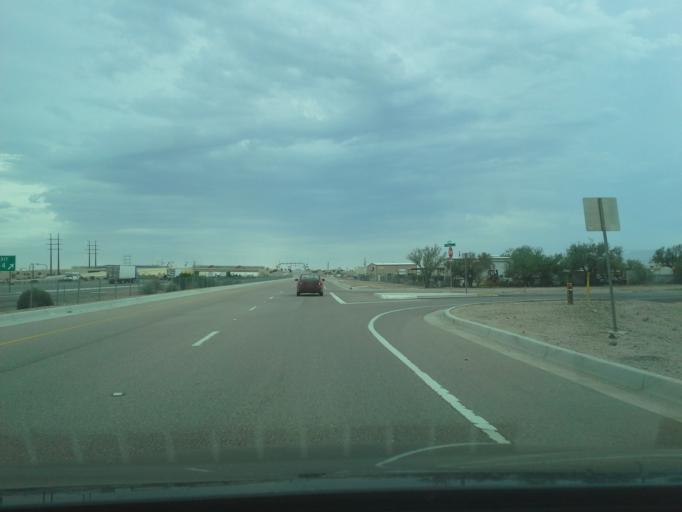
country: US
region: Arizona
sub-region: Pima County
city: Tortolita
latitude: 32.3841
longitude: -111.1143
